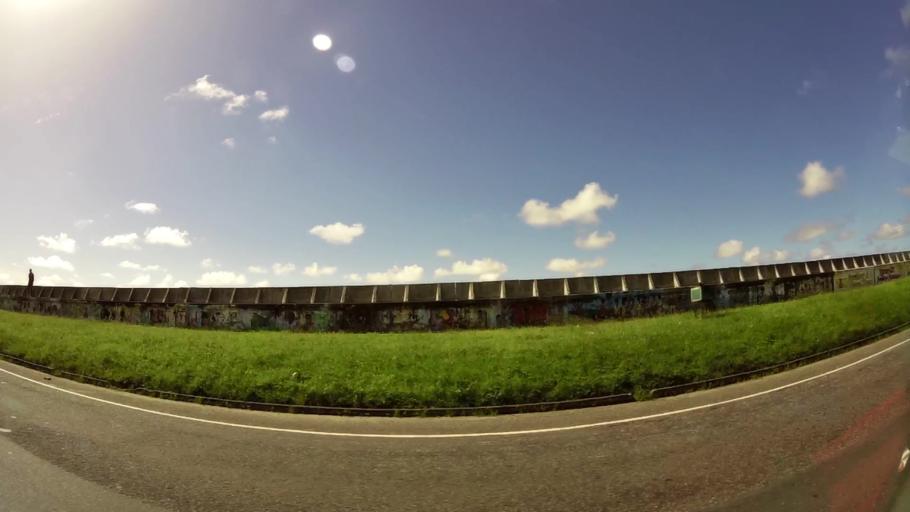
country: GY
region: Demerara-Mahaica
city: Georgetown
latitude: 6.8260
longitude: -58.1302
